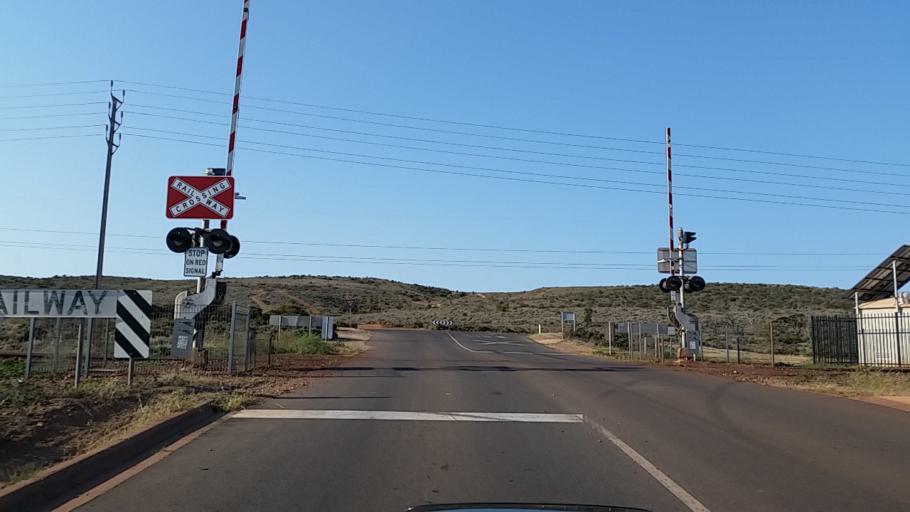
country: AU
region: South Australia
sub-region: Whyalla
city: Whyalla
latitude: -33.0079
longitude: 137.5321
